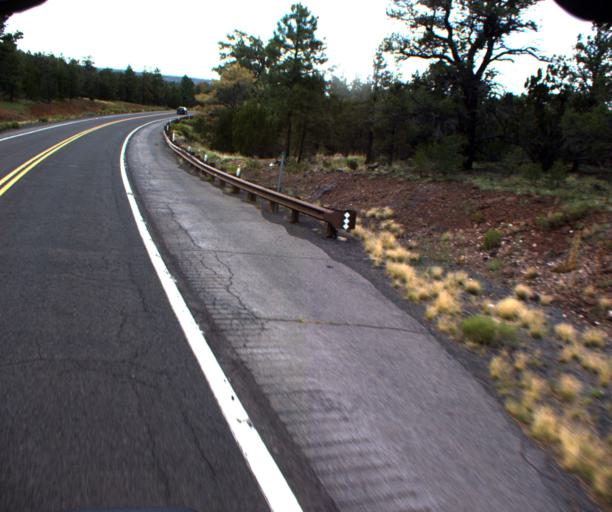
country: US
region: Arizona
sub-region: Coconino County
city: Parks
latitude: 35.5158
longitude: -111.8350
